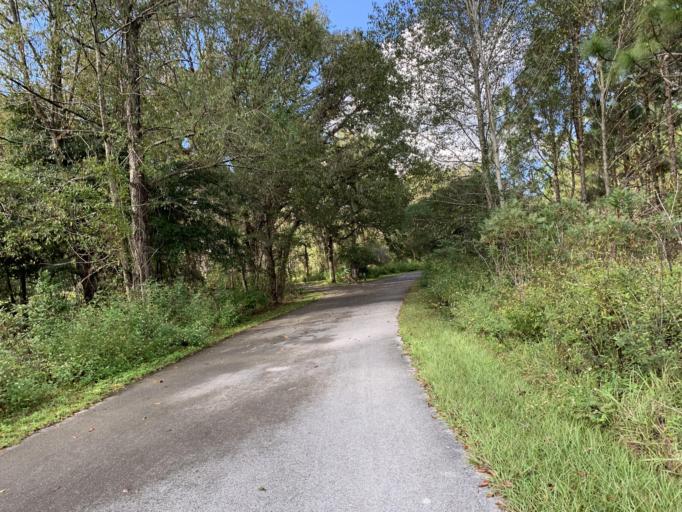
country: US
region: Florida
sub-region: Marion County
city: Silver Springs Shores
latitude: 29.1501
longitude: -82.0453
